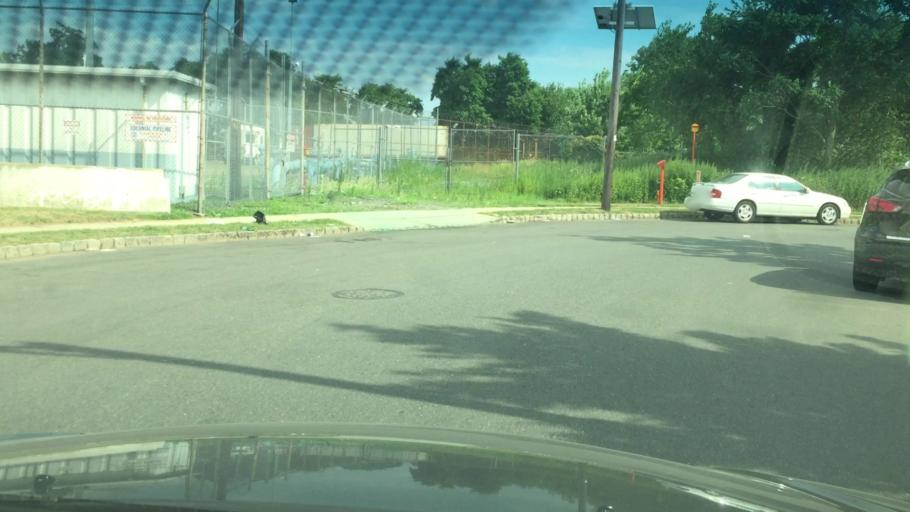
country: US
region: New Jersey
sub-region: Union County
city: Elizabeth
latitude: 40.6506
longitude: -74.1807
